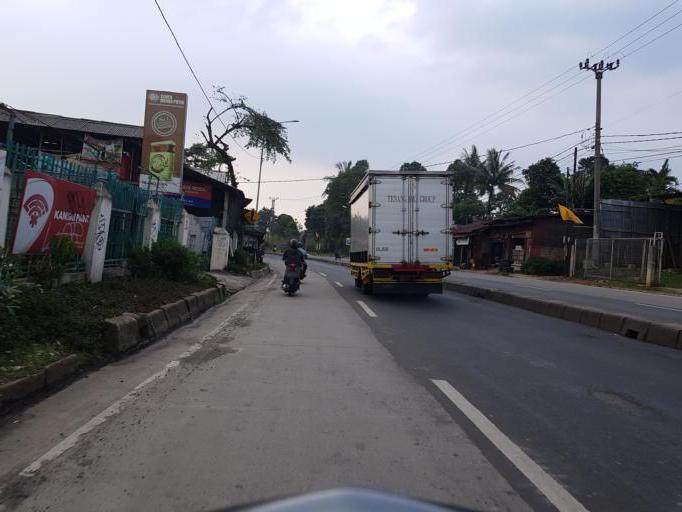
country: ID
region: West Java
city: Parung
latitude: -6.4944
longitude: 106.7507
